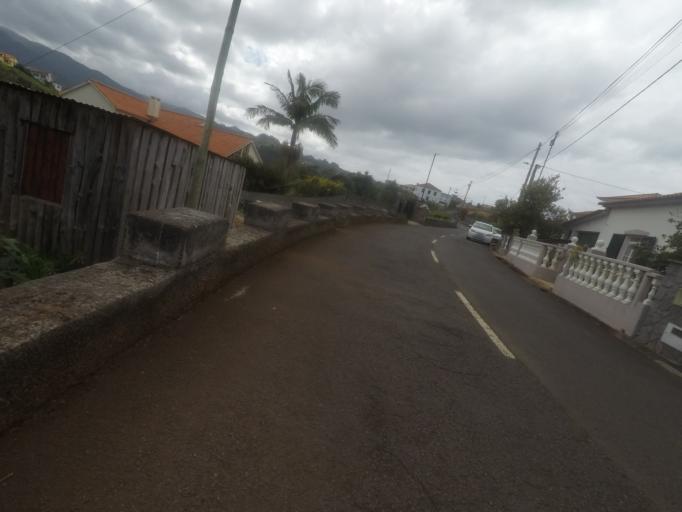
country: PT
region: Madeira
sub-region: Santana
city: Santana
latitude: 32.8237
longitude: -16.8873
